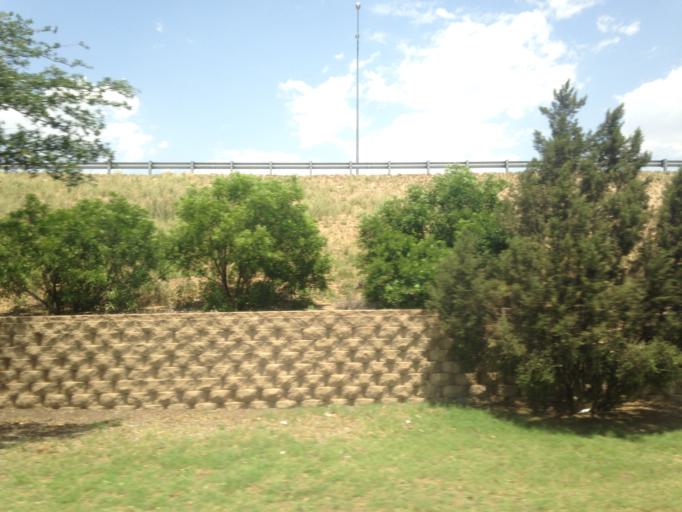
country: US
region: Texas
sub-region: Midland County
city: Midland
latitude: 32.0332
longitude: -102.1286
